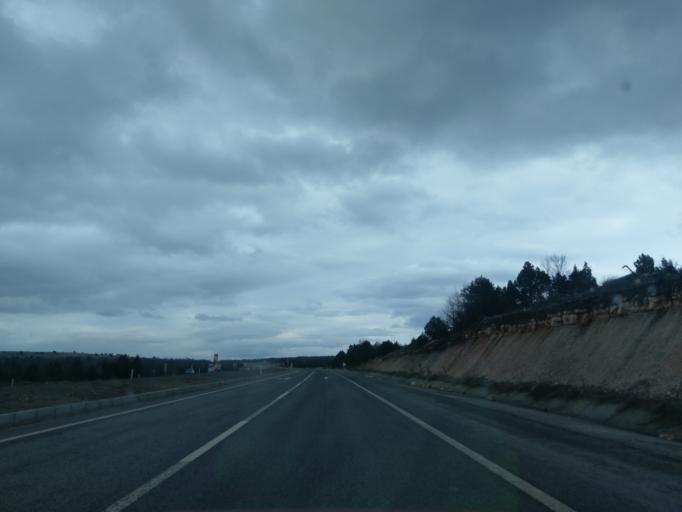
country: TR
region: Kuetahya
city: Cavdarhisar
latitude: 39.2227
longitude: 29.7427
